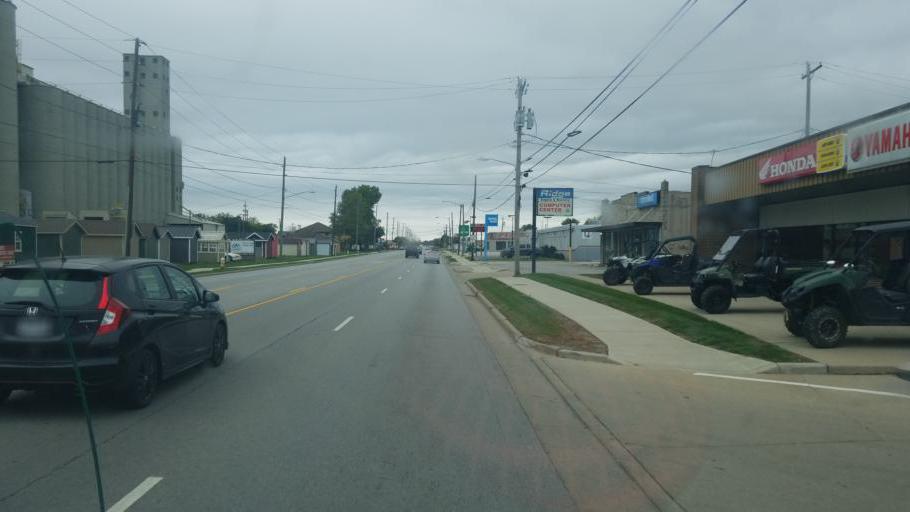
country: US
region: Ohio
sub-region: Lucas County
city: Maumee
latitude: 41.5707
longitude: -83.6581
